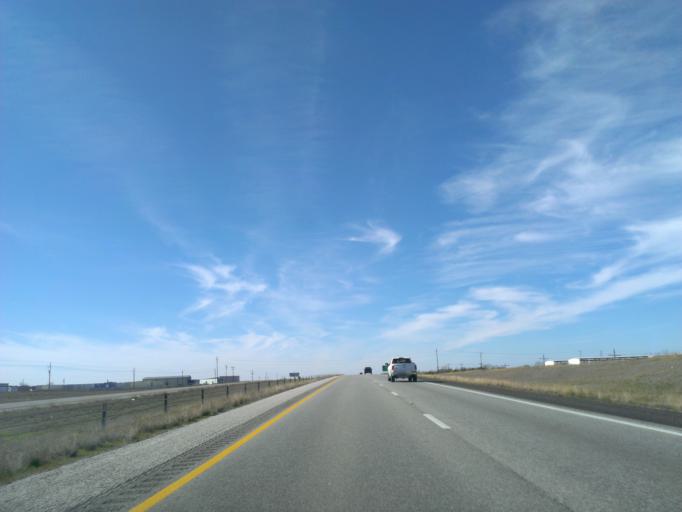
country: US
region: Texas
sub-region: Bell County
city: Nolanville
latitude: 31.0699
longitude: -97.5865
